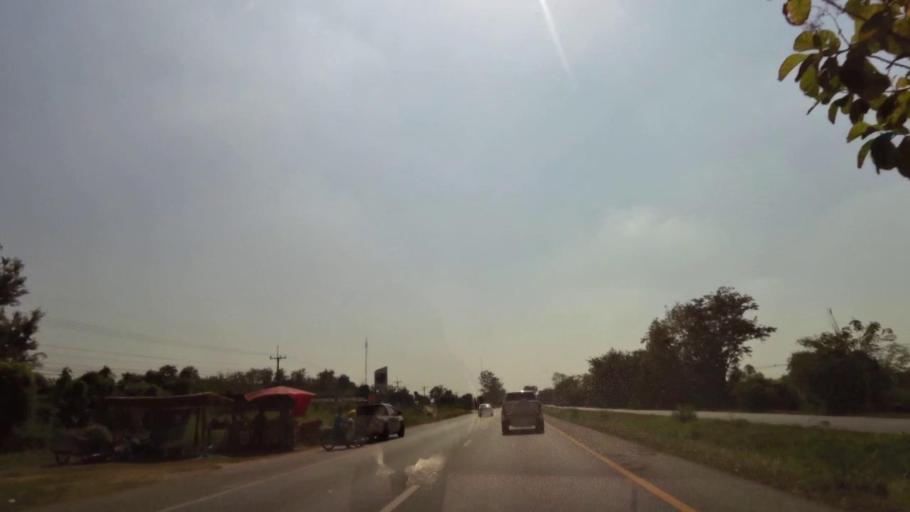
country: TH
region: Phichit
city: Wachira Barami
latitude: 16.4233
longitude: 100.1442
